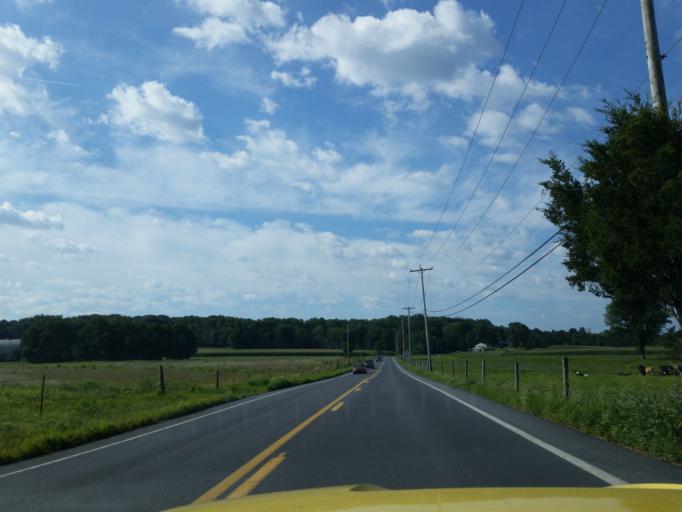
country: US
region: Pennsylvania
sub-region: Lebanon County
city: Sand Hill
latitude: 40.3790
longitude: -76.4120
